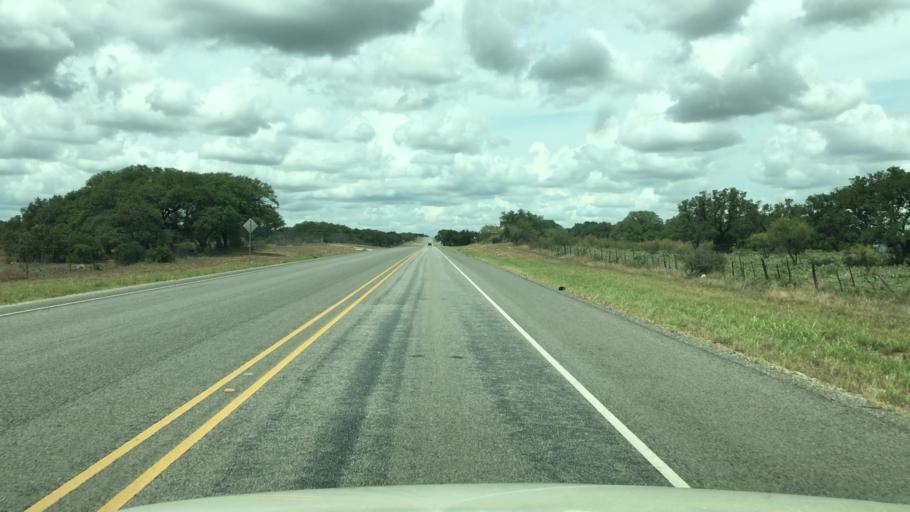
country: US
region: Texas
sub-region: McCulloch County
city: Brady
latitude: 31.0233
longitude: -99.2189
